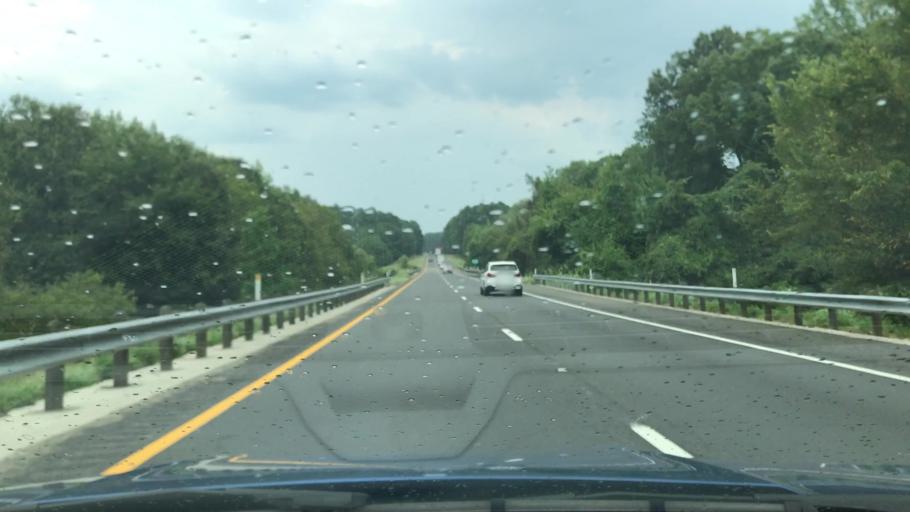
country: US
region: Texas
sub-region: Harrison County
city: Marshall
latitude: 32.4872
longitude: -94.4453
